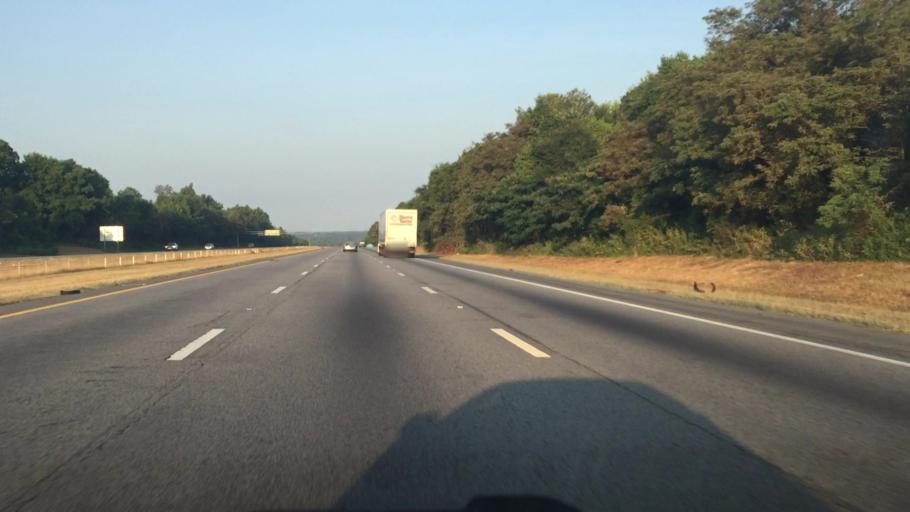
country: US
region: North Carolina
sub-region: Randolph County
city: Trinity
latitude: 35.8930
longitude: -79.9790
